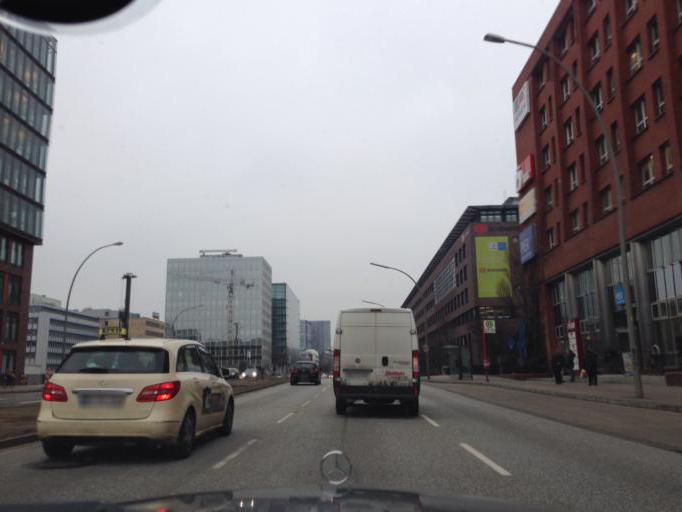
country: DE
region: Hamburg
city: Hammerbrook
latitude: 53.5456
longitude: 10.0304
